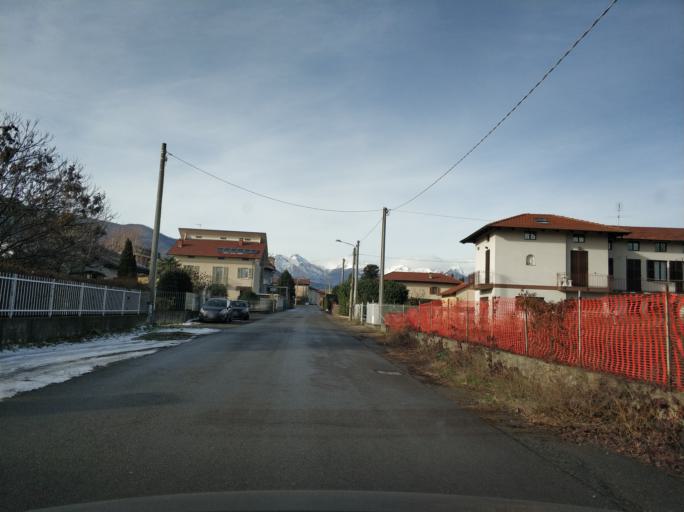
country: IT
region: Piedmont
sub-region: Provincia di Torino
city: Mathi
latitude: 45.2594
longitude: 7.5469
